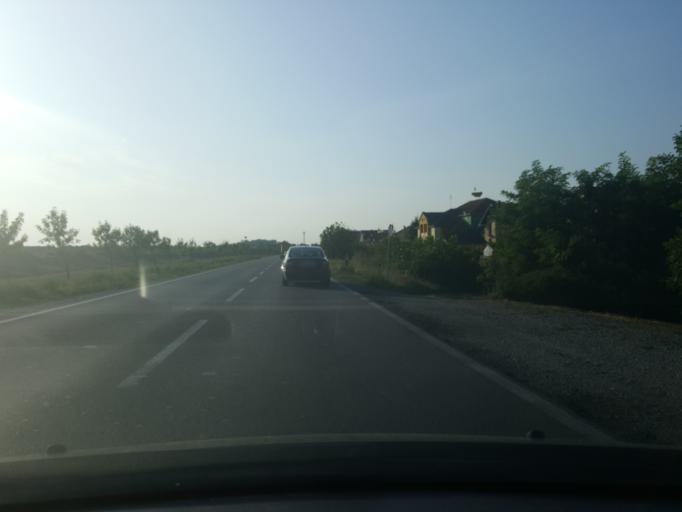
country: RS
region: Central Serbia
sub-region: Macvanski Okrug
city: Sabac
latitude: 44.7443
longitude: 19.6694
